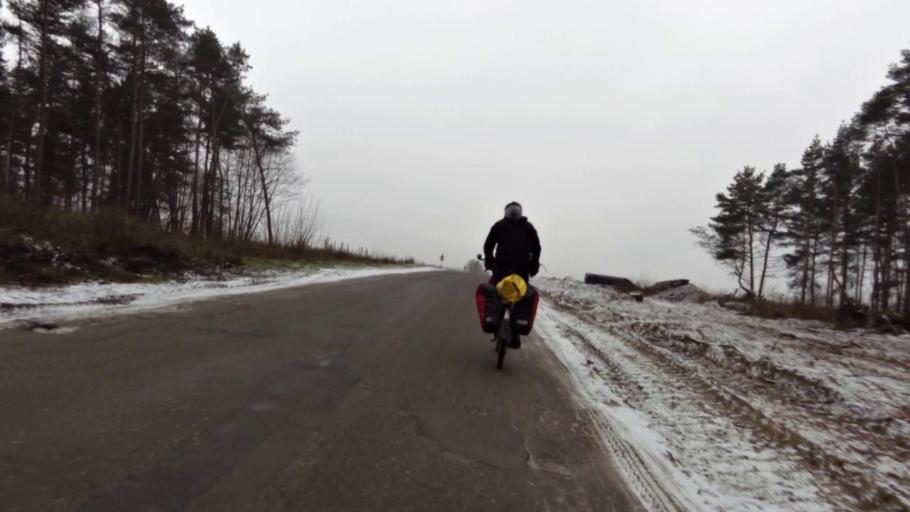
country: PL
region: West Pomeranian Voivodeship
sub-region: Powiat walecki
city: Walcz
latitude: 53.2965
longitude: 16.4772
